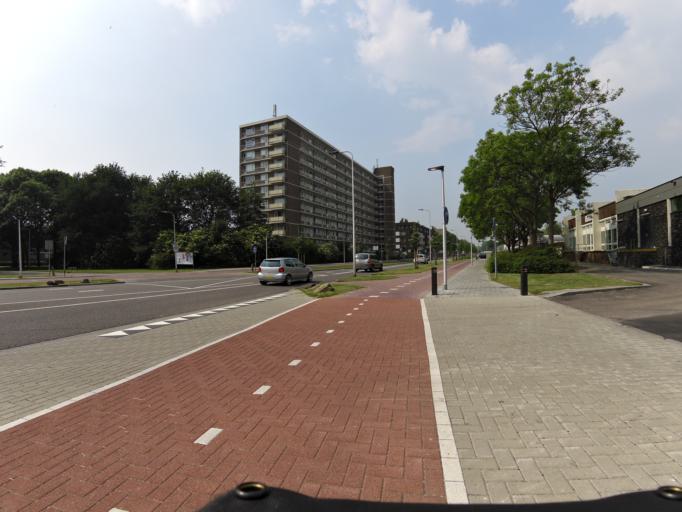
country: NL
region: South Holland
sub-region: Gemeente Spijkenisse
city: Spijkenisse
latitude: 51.8525
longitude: 4.3175
